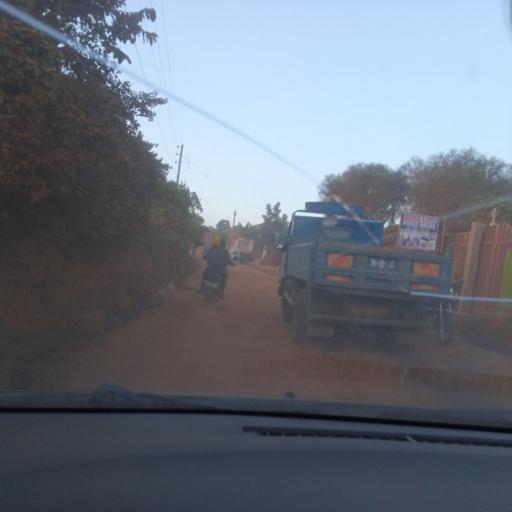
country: UG
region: Central Region
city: Masaka
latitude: -0.3188
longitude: 31.7680
